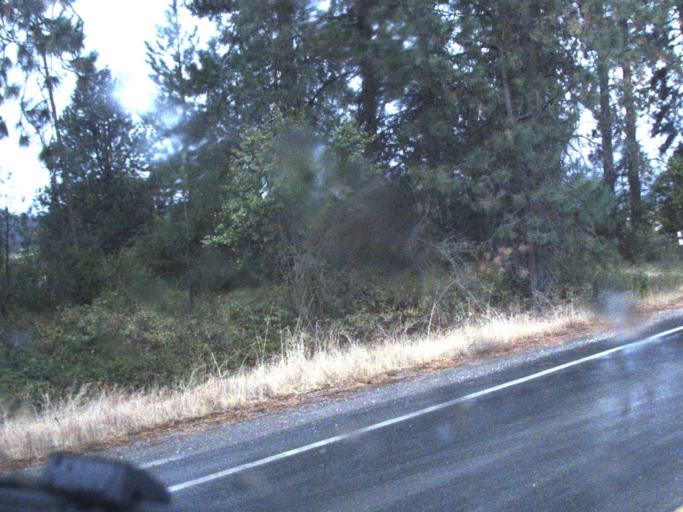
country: US
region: Washington
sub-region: Stevens County
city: Chewelah
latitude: 48.1593
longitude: -117.7258
